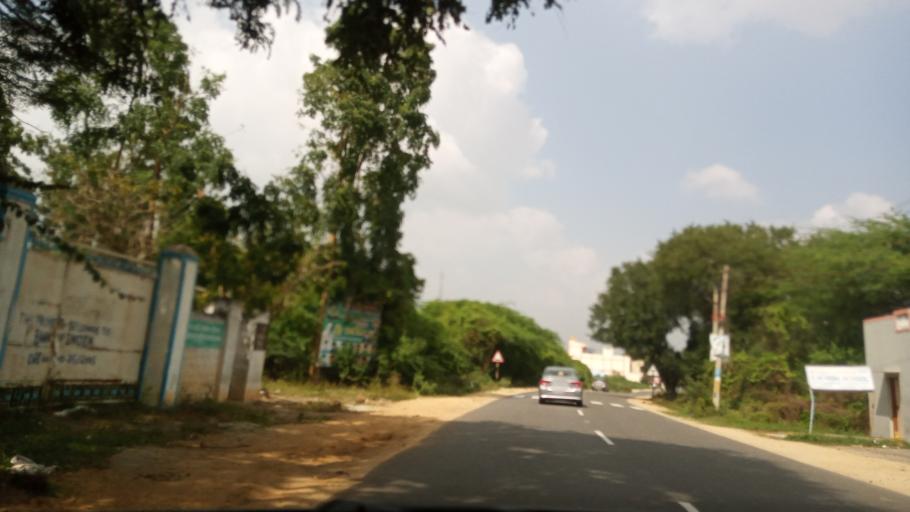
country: IN
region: Andhra Pradesh
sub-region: Chittoor
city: Madanapalle
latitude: 13.6361
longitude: 78.5543
